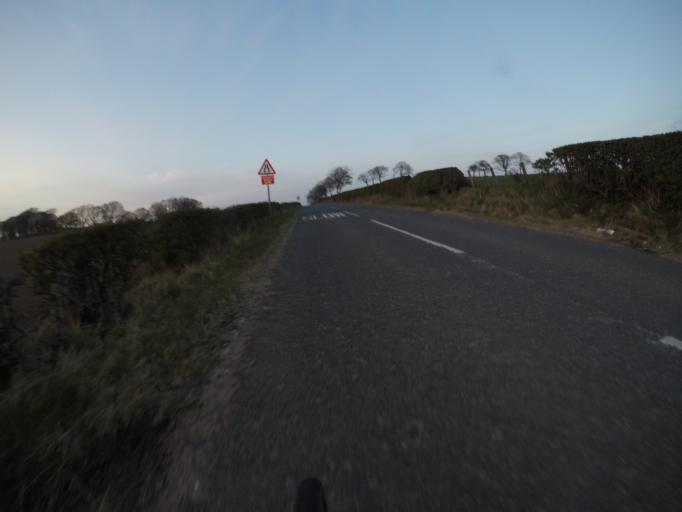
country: GB
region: Scotland
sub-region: South Ayrshire
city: Dundonald
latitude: 55.5606
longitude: -4.6086
